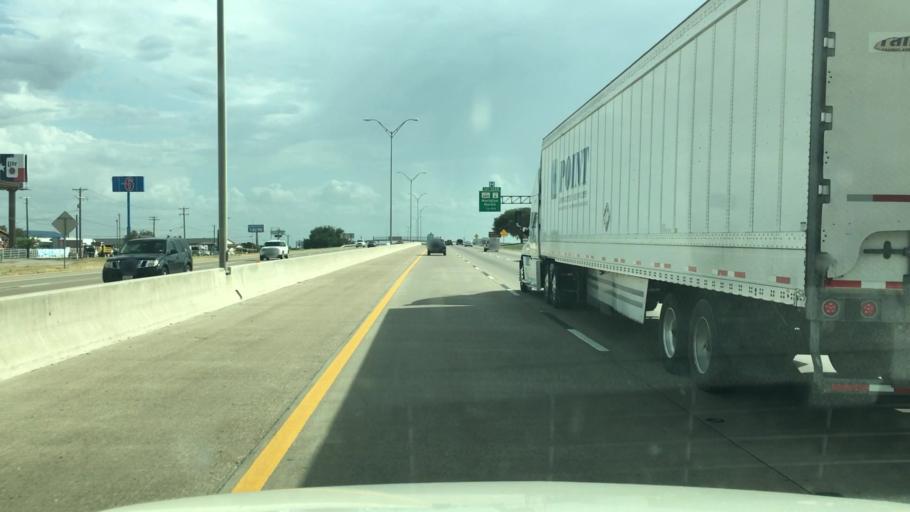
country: US
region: Texas
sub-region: McLennan County
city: Beverly
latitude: 31.5121
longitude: -97.1406
